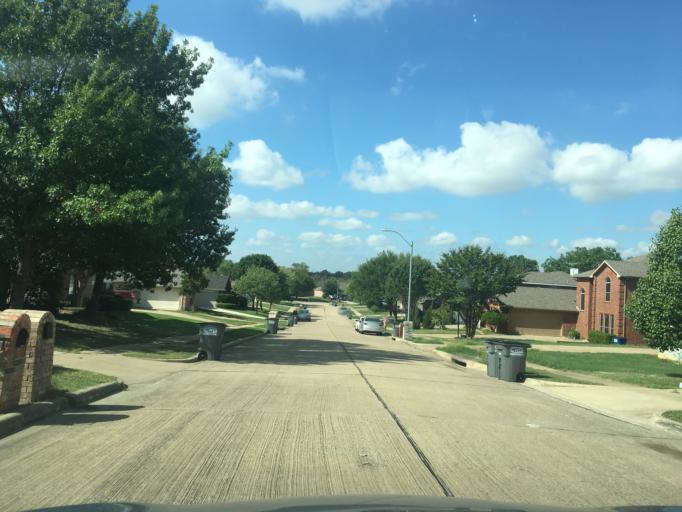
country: US
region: Texas
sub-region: Dallas County
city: Sachse
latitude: 32.9565
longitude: -96.5874
